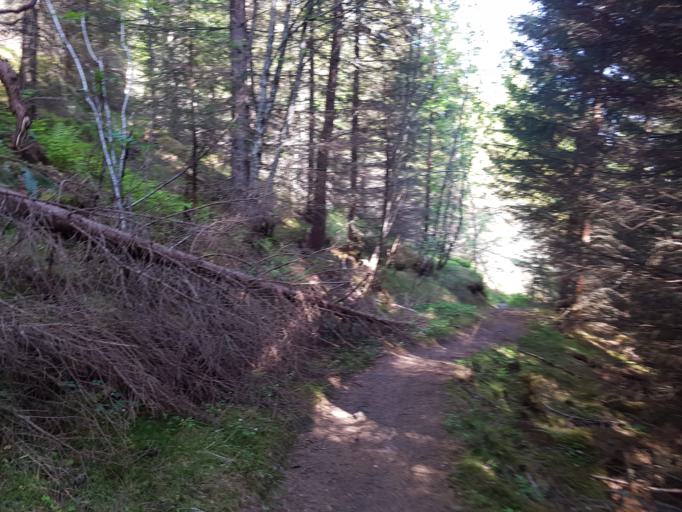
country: NO
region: Sor-Trondelag
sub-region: Trondheim
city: Trondheim
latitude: 63.4292
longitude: 10.3378
